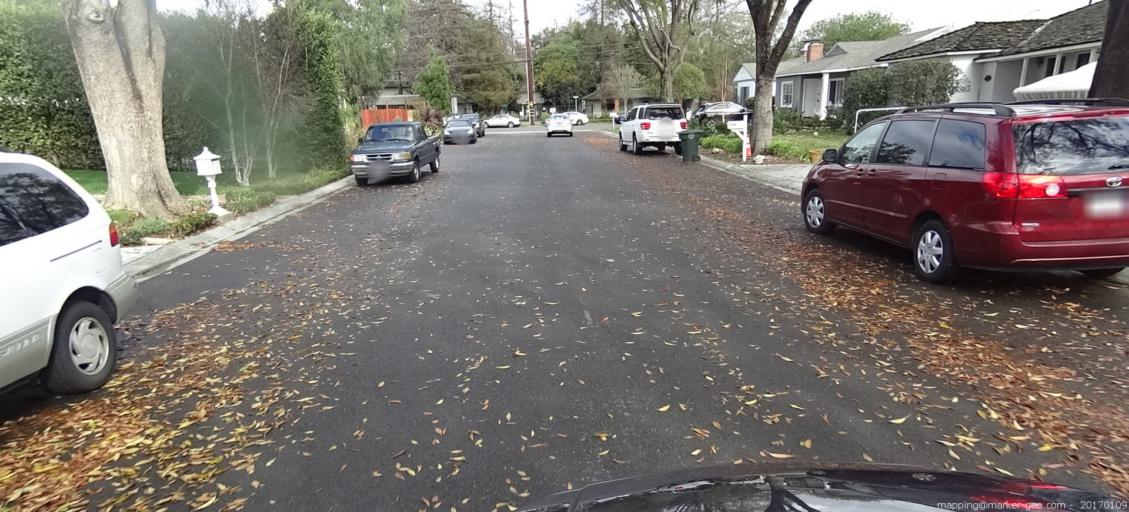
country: US
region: California
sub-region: Orange County
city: Costa Mesa
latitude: 33.6596
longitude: -117.8870
